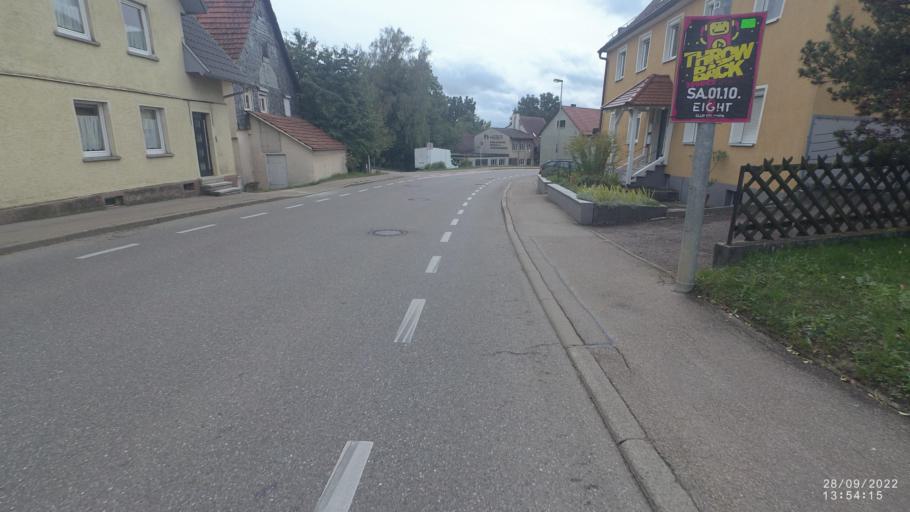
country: DE
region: Baden-Wuerttemberg
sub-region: Regierungsbezirk Stuttgart
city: Wangen
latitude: 48.7281
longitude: 9.6101
